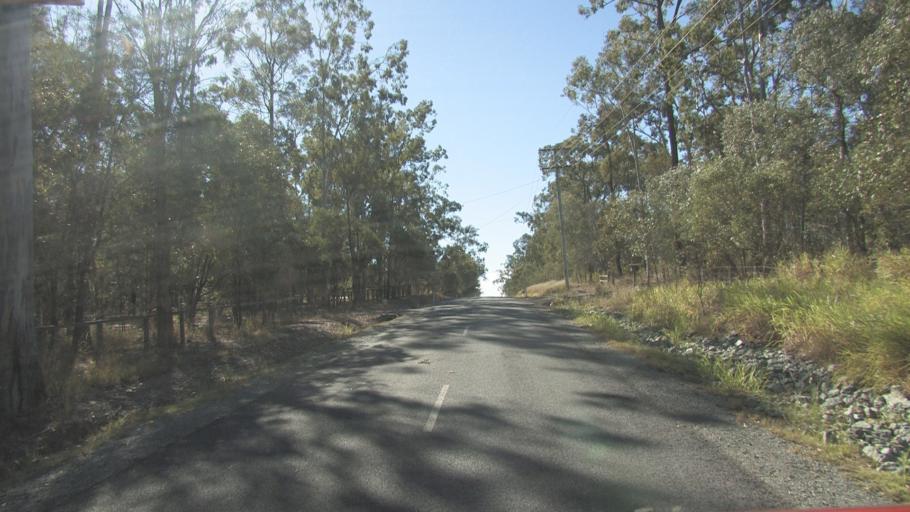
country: AU
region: Queensland
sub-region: Logan
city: Chambers Flat
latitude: -27.8127
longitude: 153.0715
